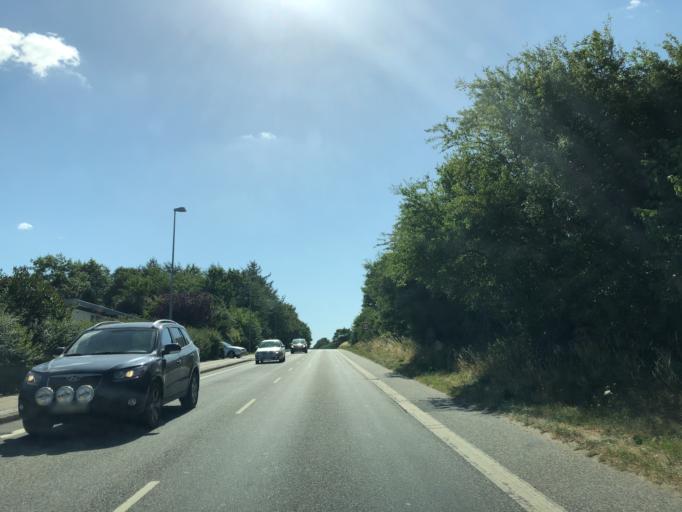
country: DK
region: North Denmark
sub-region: Mariagerfjord Kommune
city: Hobro
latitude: 56.6331
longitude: 9.7661
